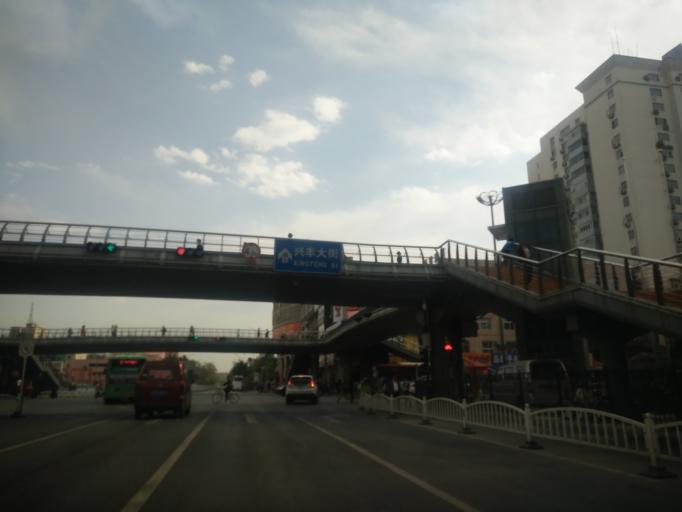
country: CN
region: Beijing
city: Xingfeng
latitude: 39.7309
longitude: 116.3333
